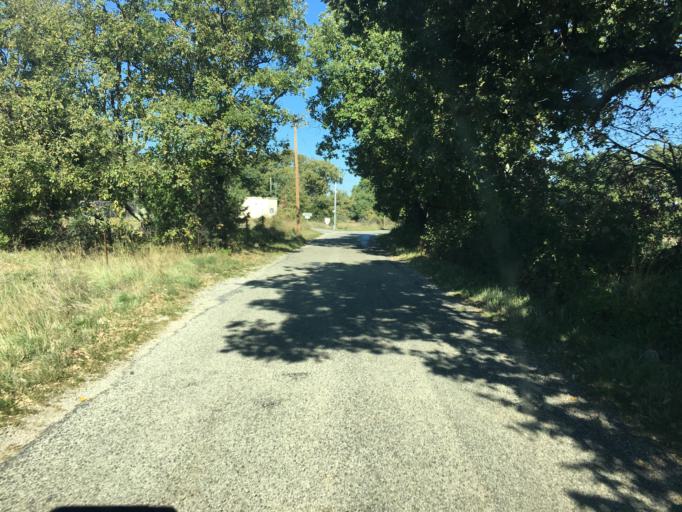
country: FR
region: Languedoc-Roussillon
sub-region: Departement du Gard
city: Montaren-et-Saint-Mediers
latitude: 44.1509
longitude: 4.3104
